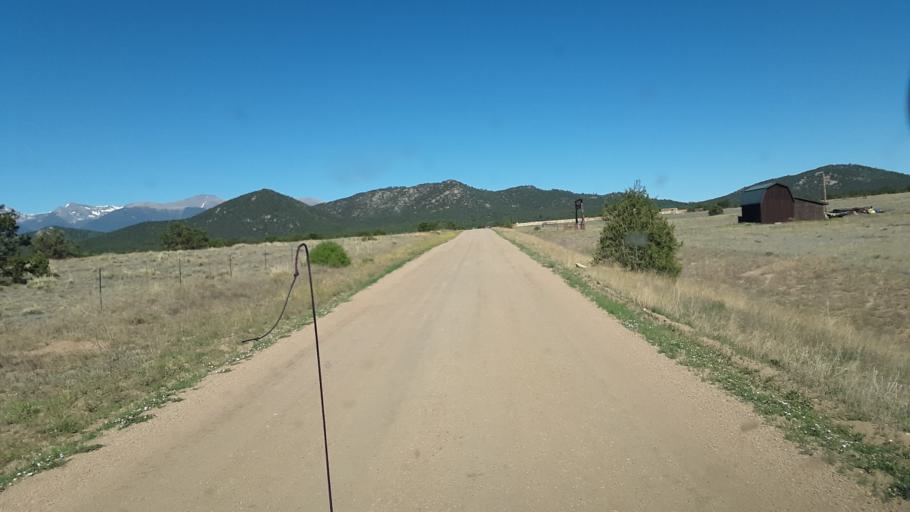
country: US
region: Colorado
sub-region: Custer County
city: Westcliffe
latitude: 38.2850
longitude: -105.5150
